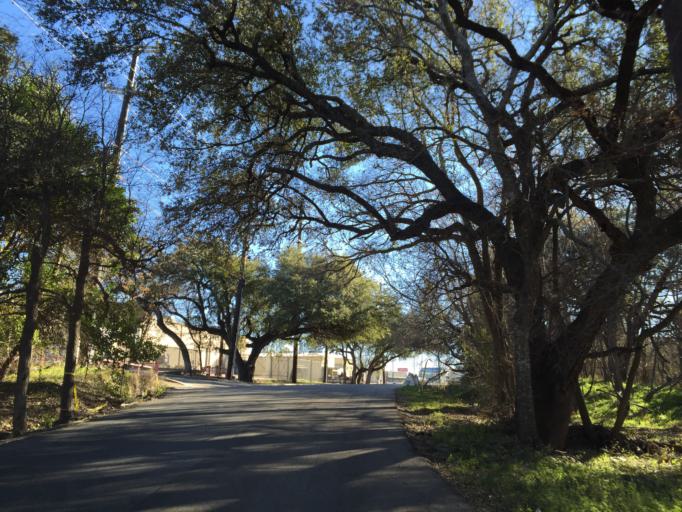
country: US
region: Texas
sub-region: Bexar County
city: Castle Hills
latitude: 29.5540
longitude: -98.4881
